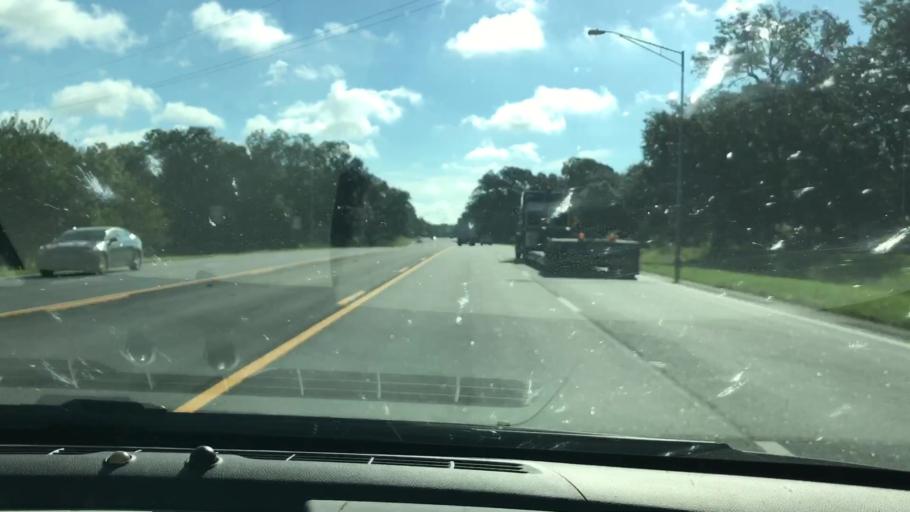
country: US
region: Georgia
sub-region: Dougherty County
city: Albany
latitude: 31.5799
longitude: -84.0804
